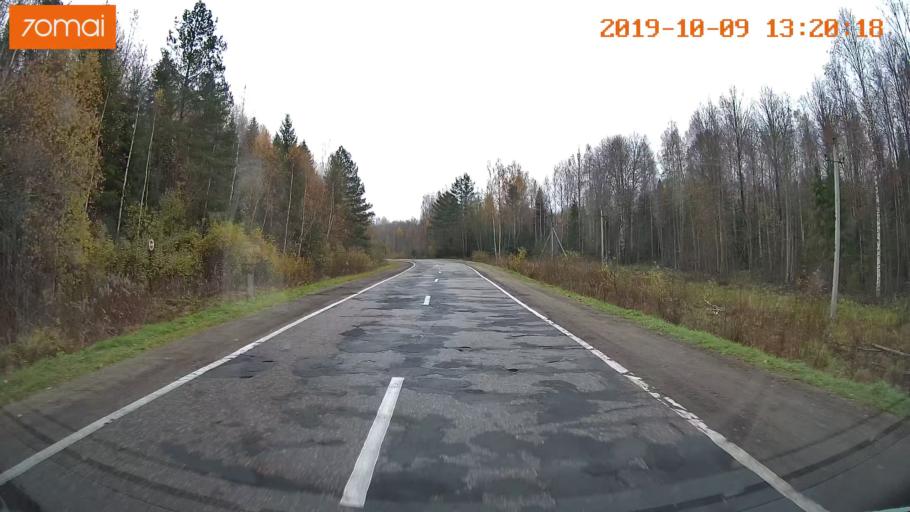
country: RU
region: Jaroslavl
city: Lyubim
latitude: 58.3437
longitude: 40.8275
